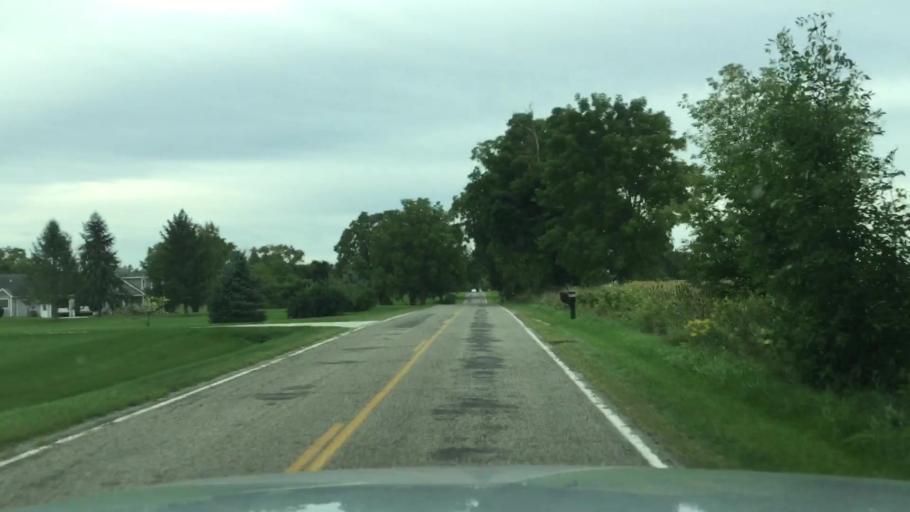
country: US
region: Michigan
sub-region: Shiawassee County
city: Durand
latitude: 42.8969
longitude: -84.0691
